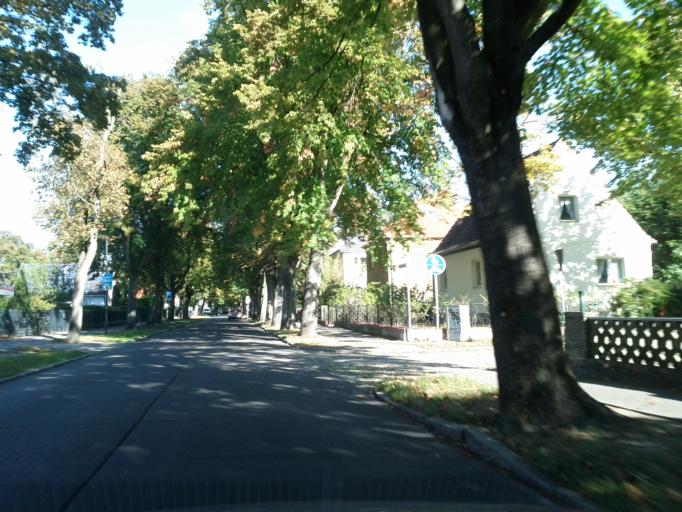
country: DE
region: Brandenburg
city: Schoneiche
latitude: 52.4622
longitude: 13.6992
